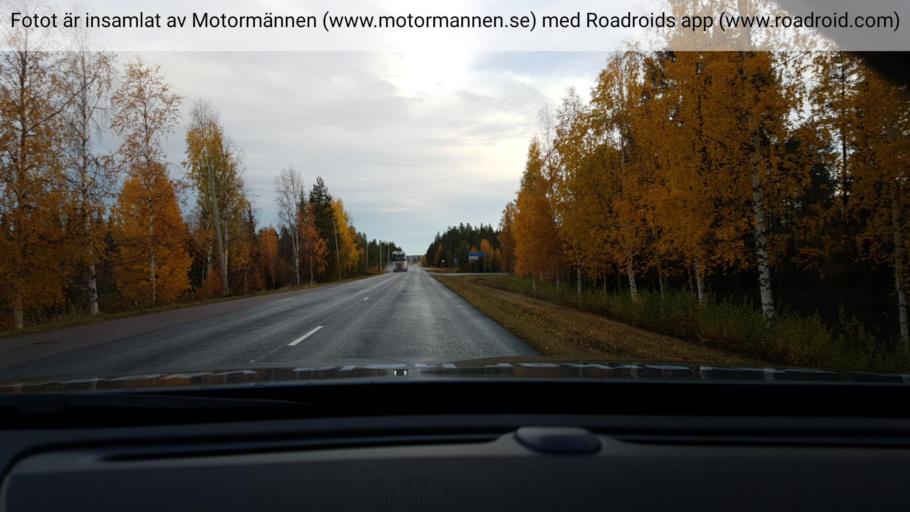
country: SE
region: Norrbotten
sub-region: Overkalix Kommun
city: OEverkalix
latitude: 66.9471
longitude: 22.7159
